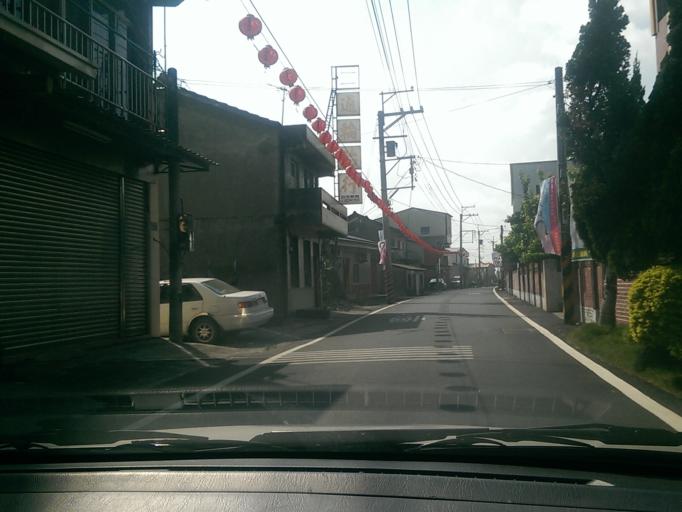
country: TW
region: Taiwan
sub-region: Changhua
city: Chang-hua
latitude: 23.9643
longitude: 120.5237
